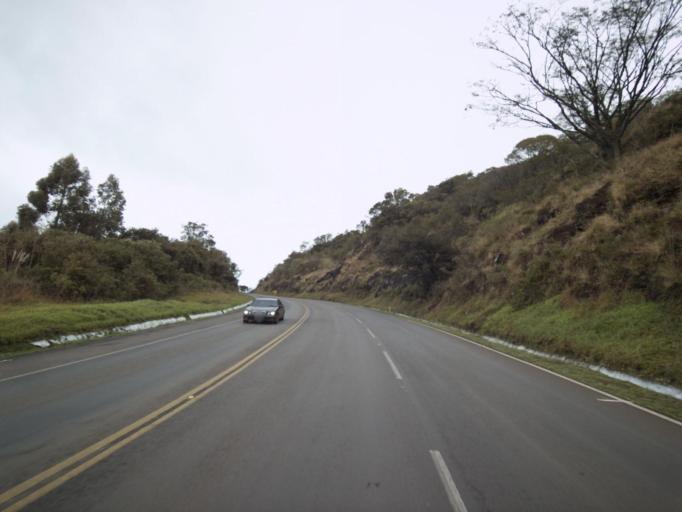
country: BR
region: Santa Catarina
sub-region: Concordia
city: Concordia
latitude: -27.0571
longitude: -51.8903
